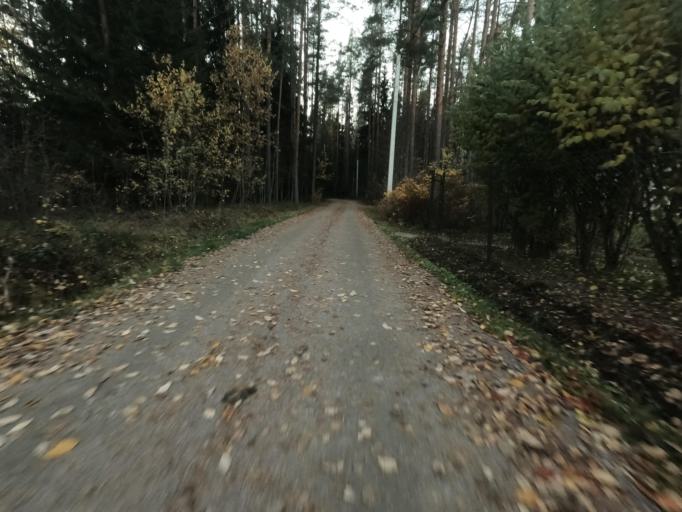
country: RU
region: St.-Petersburg
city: Komarovo
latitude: 60.2009
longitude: 29.8227
